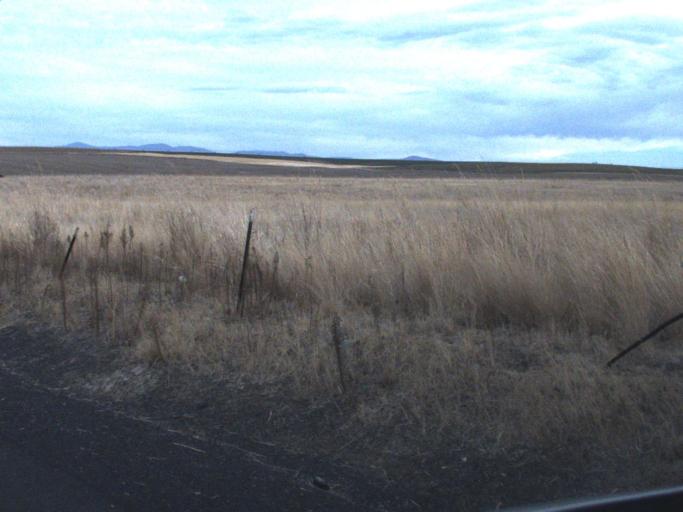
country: US
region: Washington
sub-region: Okanogan County
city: Coulee Dam
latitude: 47.7106
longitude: -118.7221
